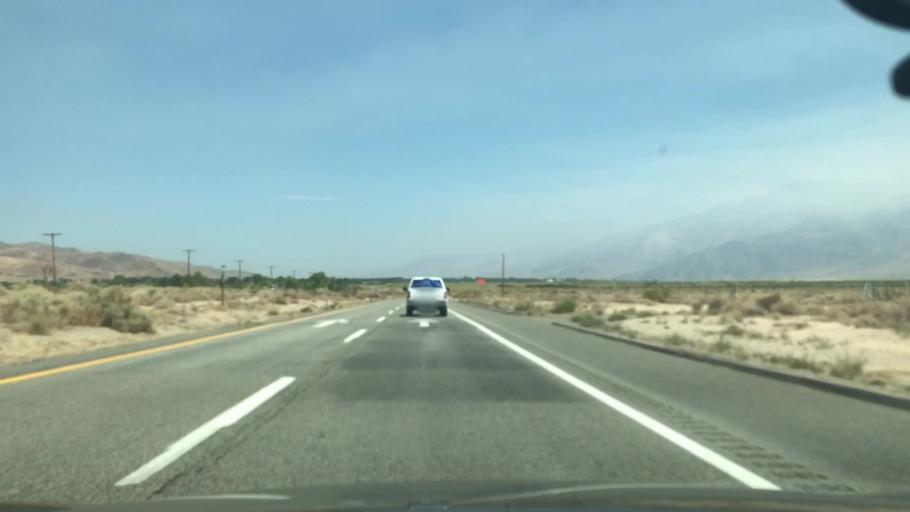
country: US
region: California
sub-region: Inyo County
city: Lone Pine
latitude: 36.5549
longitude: -118.0494
